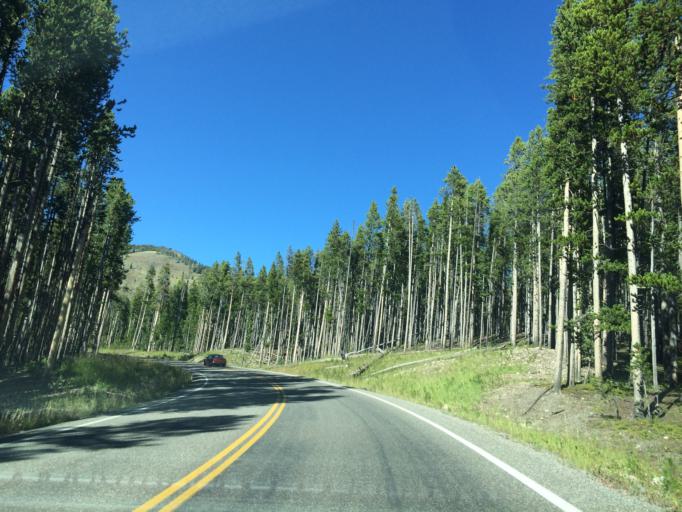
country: US
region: Montana
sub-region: Gallatin County
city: West Yellowstone
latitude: 44.7530
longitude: -110.4821
